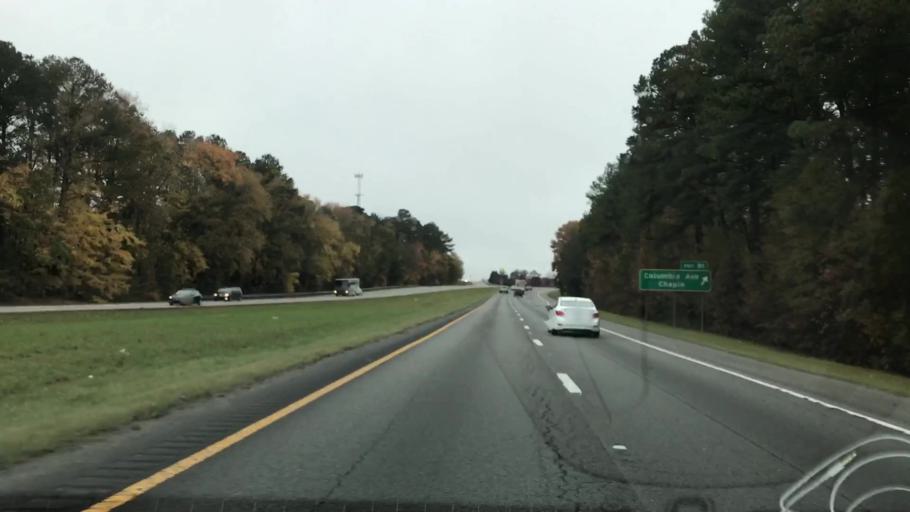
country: US
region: South Carolina
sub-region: Lexington County
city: Chapin
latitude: 34.1748
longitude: -81.3162
